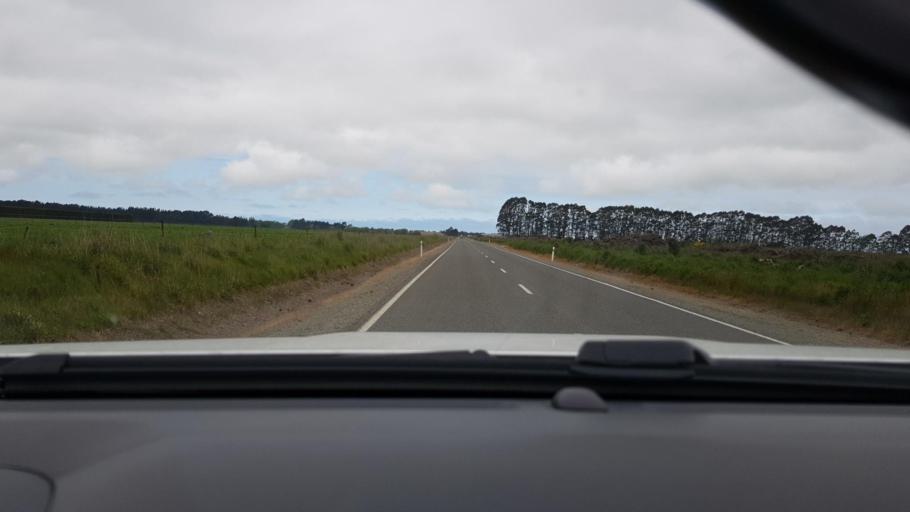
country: NZ
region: Otago
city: Oamaru
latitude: -44.9645
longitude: 171.0525
